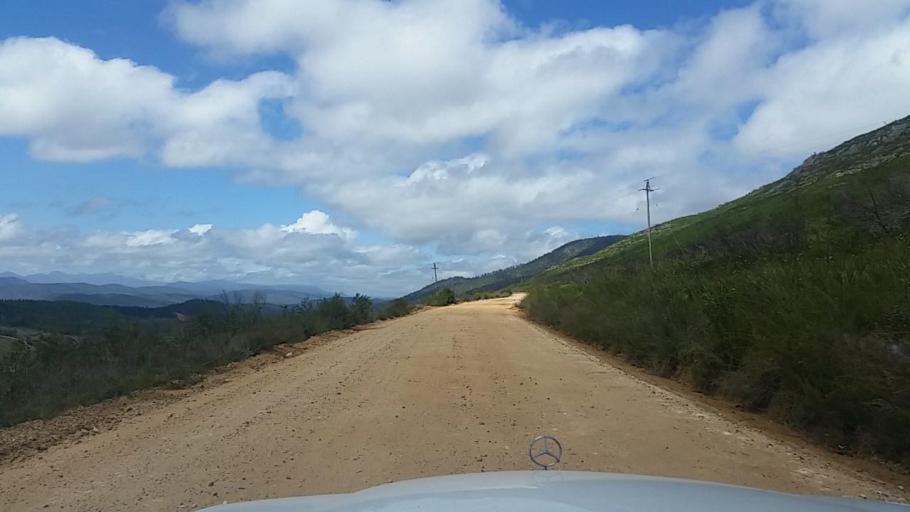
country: ZA
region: Western Cape
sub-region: Eden District Municipality
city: Knysna
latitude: -33.8878
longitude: 23.1642
